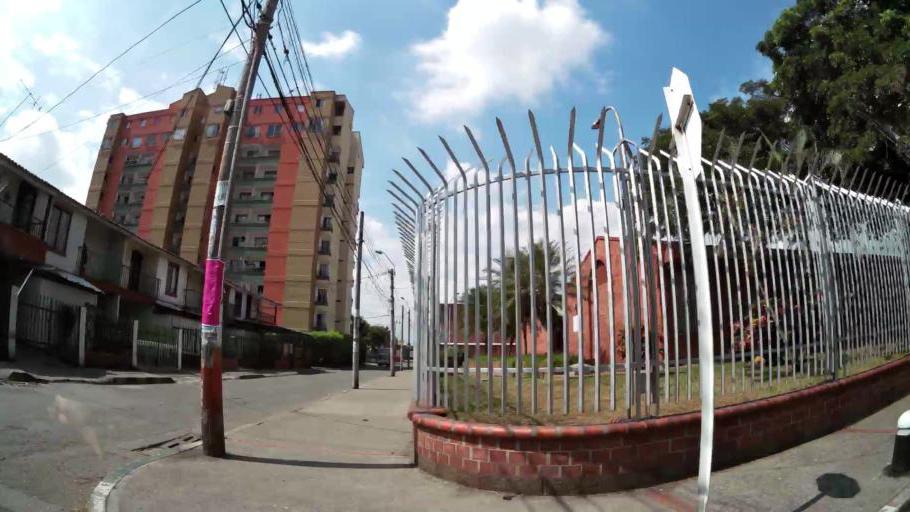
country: CO
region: Valle del Cauca
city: Cali
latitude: 3.4889
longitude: -76.5009
